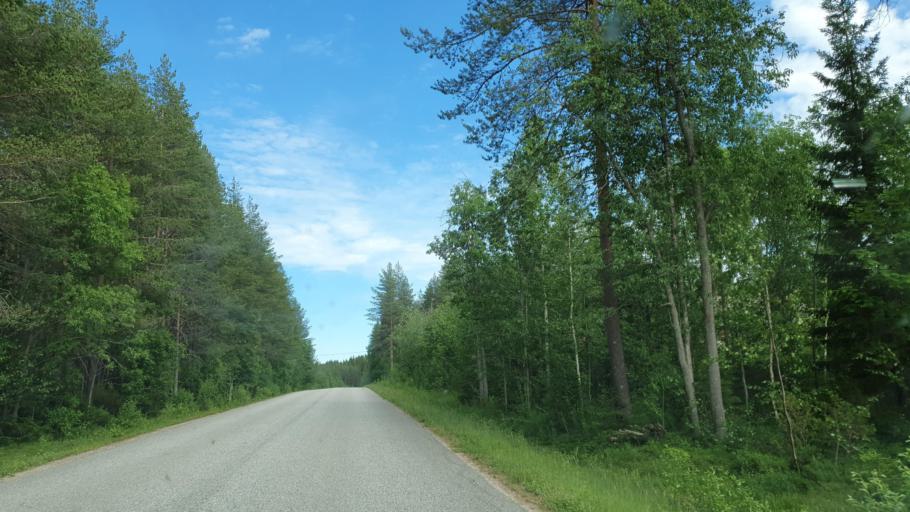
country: FI
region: Kainuu
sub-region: Kehys-Kainuu
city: Suomussalmi
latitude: 64.5533
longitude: 29.1943
